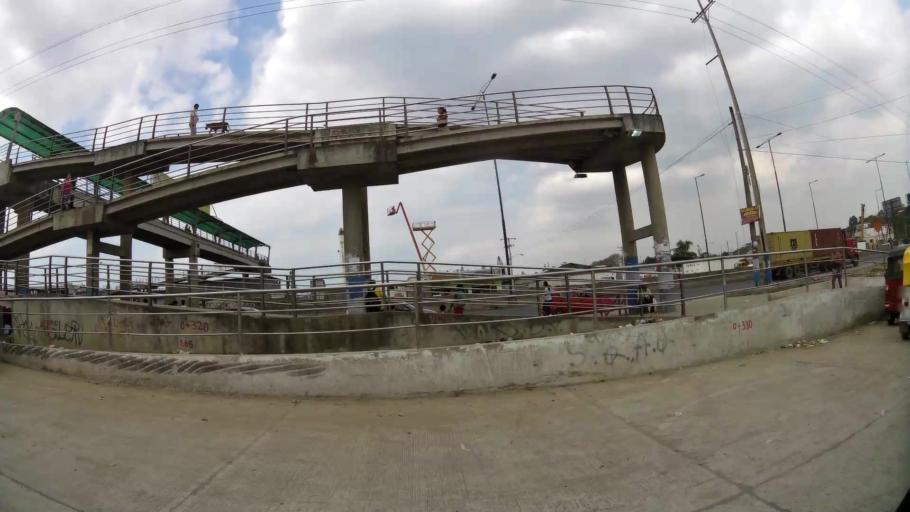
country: EC
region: Guayas
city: Santa Lucia
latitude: -2.1138
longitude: -79.9480
